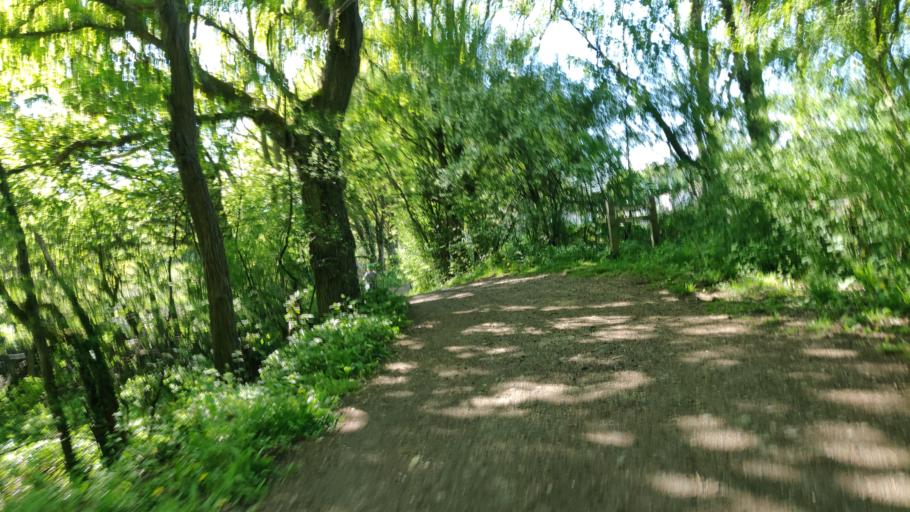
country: GB
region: England
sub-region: West Sussex
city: Rudgwick
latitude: 51.0653
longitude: -0.4042
